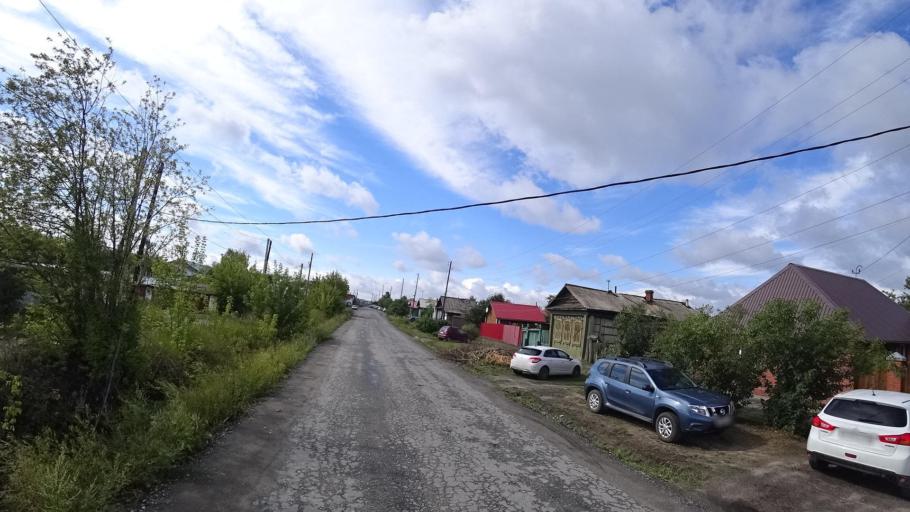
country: RU
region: Sverdlovsk
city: Kamyshlov
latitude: 56.8376
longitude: 62.7272
